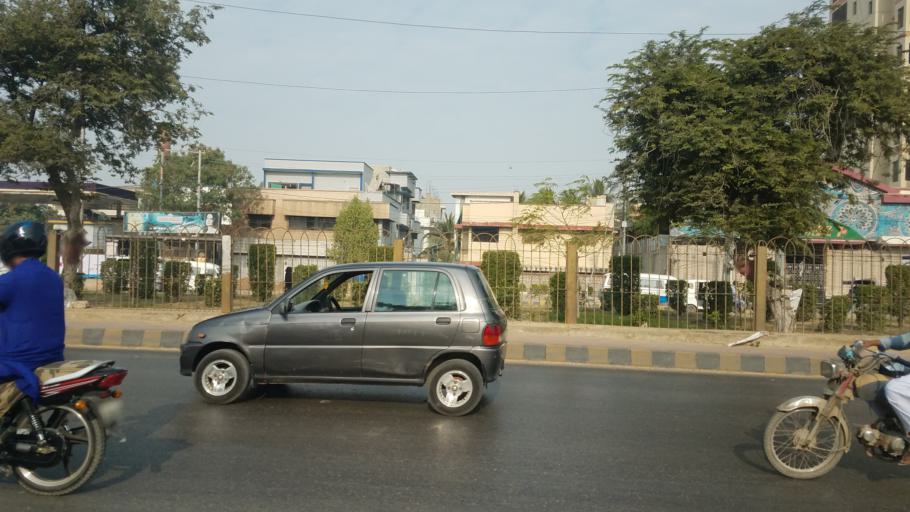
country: PK
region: Sindh
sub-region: Karachi District
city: Karachi
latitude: 24.9255
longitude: 67.0617
